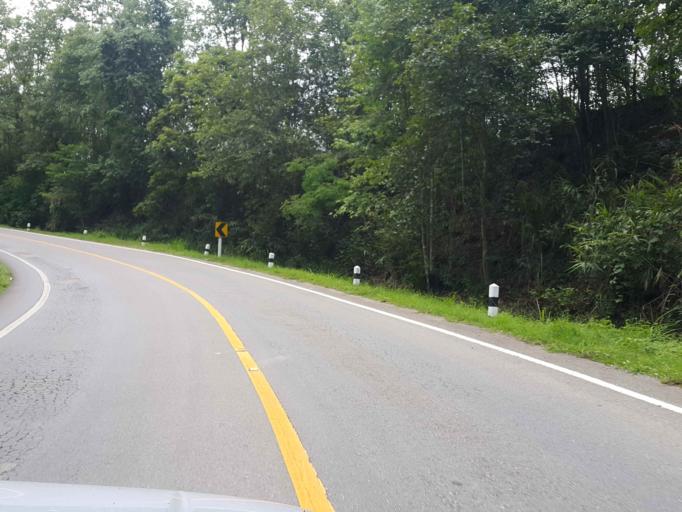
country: TH
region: Chiang Mai
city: Chom Thong
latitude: 18.5306
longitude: 98.6075
